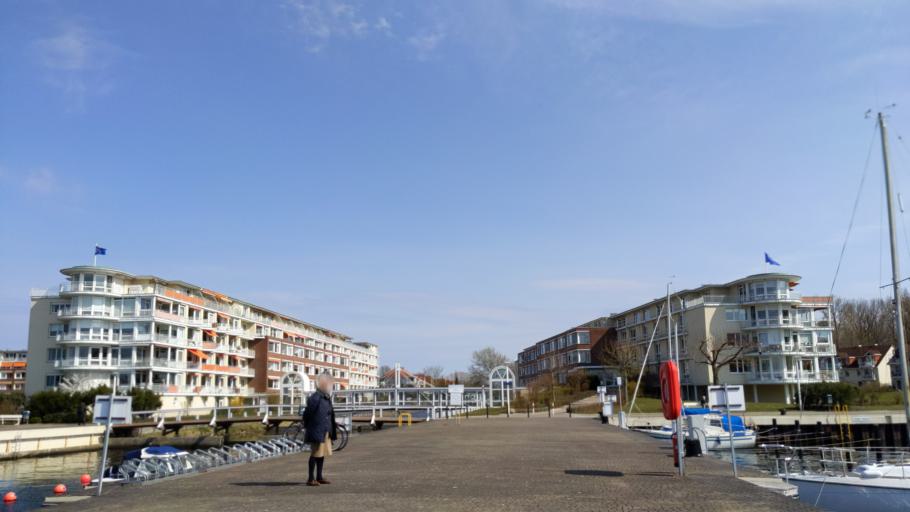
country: DE
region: Schleswig-Holstein
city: Travemuende
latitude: 53.9533
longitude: 10.8692
